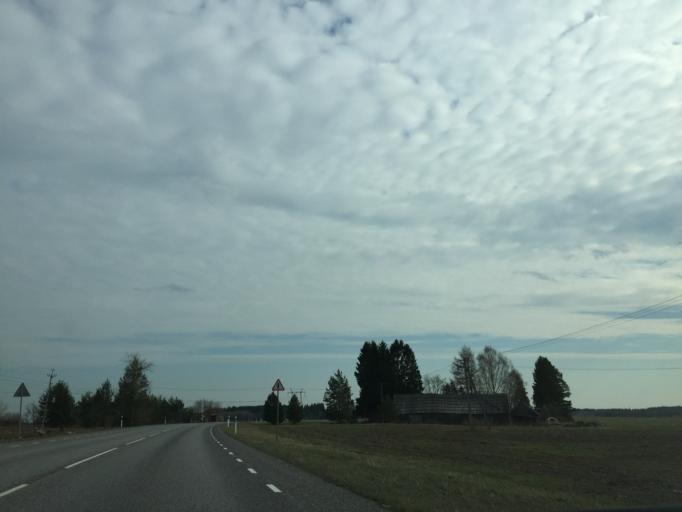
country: EE
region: Ida-Virumaa
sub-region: Johvi vald
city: Johvi
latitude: 59.3154
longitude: 27.4964
